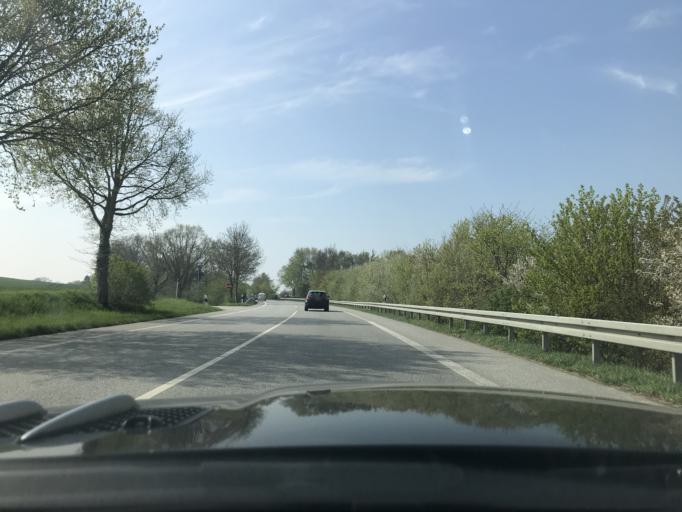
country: DE
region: Schleswig-Holstein
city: Gromitz
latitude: 54.1461
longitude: 10.9323
